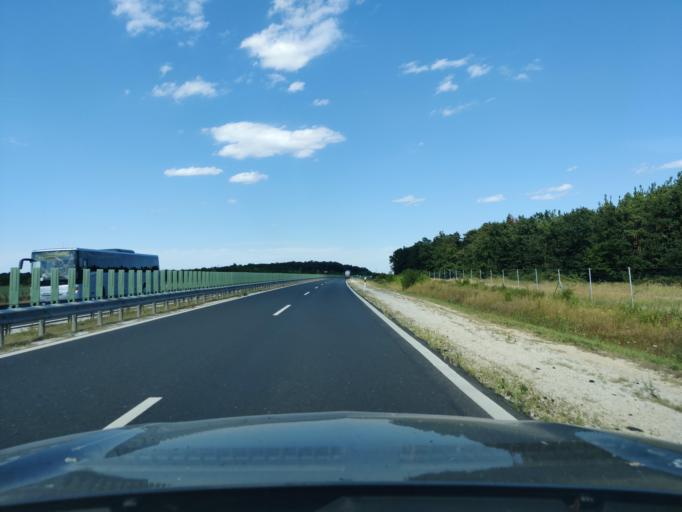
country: HU
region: Vas
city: Vep
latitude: 47.2901
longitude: 16.8191
